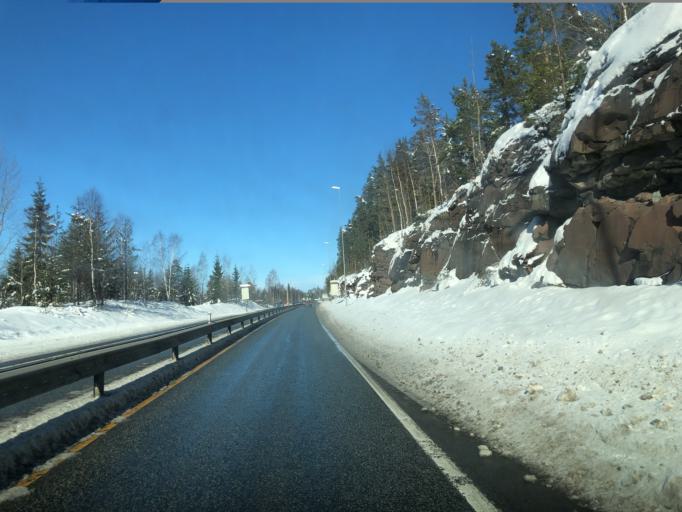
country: NO
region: Buskerud
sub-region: Hole
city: Vik
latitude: 60.0222
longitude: 10.2680
